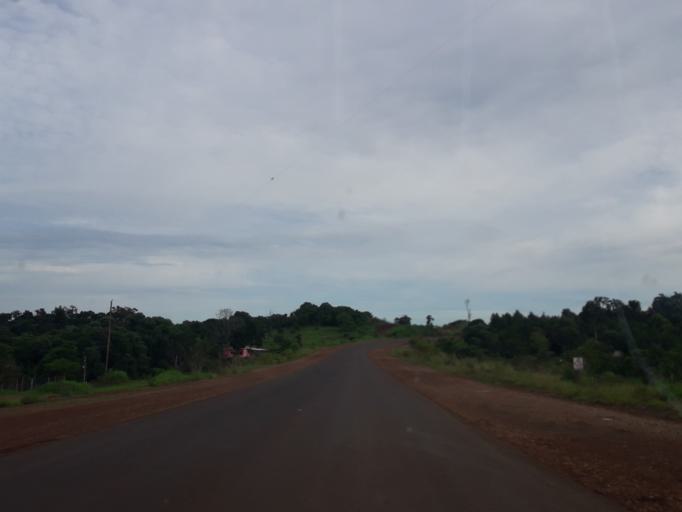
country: AR
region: Misiones
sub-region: Departamento de San Pedro
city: San Pedro
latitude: -26.5279
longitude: -53.9398
